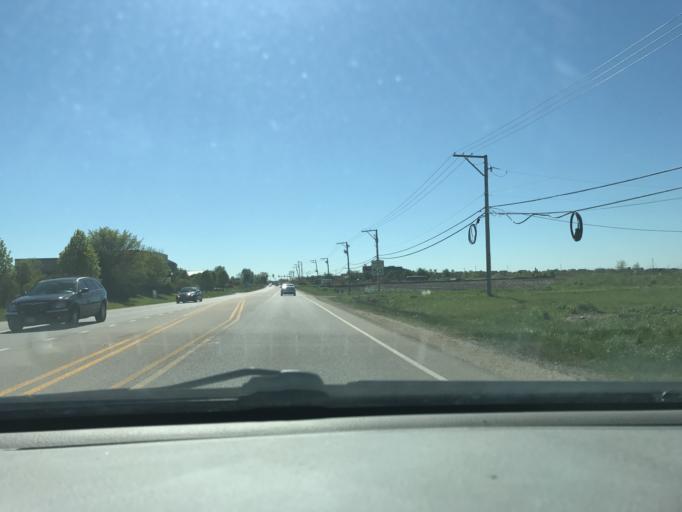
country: US
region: Illinois
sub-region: Kane County
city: Pingree Grove
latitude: 42.0407
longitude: -88.3676
